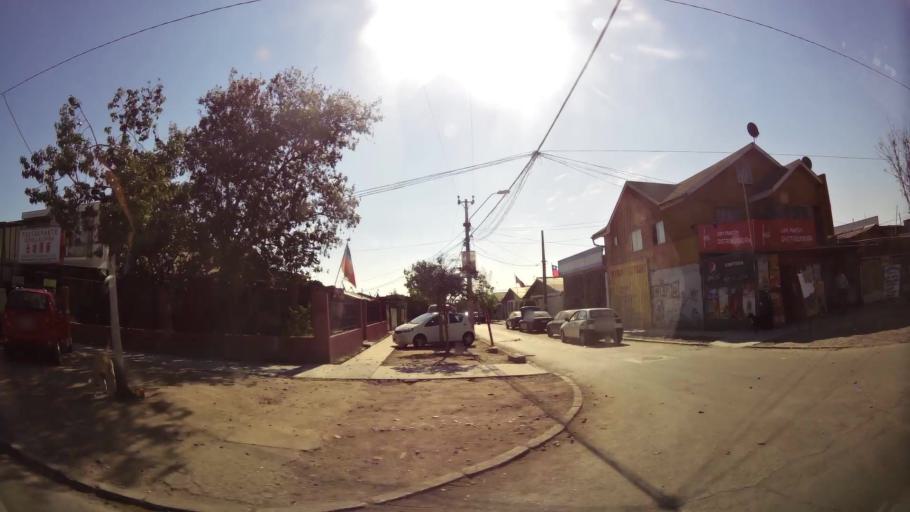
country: CL
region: Santiago Metropolitan
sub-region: Provincia de Santiago
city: Santiago
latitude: -33.5149
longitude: -70.6934
